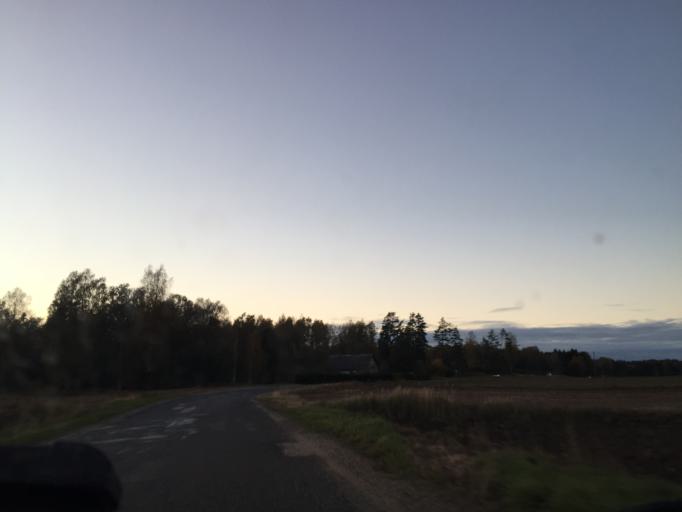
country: LV
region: Talsu Rajons
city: Sabile
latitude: 56.9661
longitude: 22.6062
